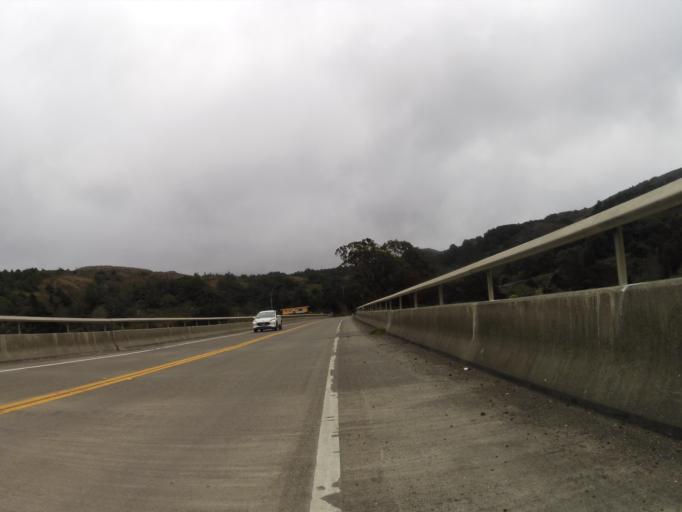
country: US
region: California
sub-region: Sonoma County
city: Monte Rio
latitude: 38.4350
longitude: -123.1020
